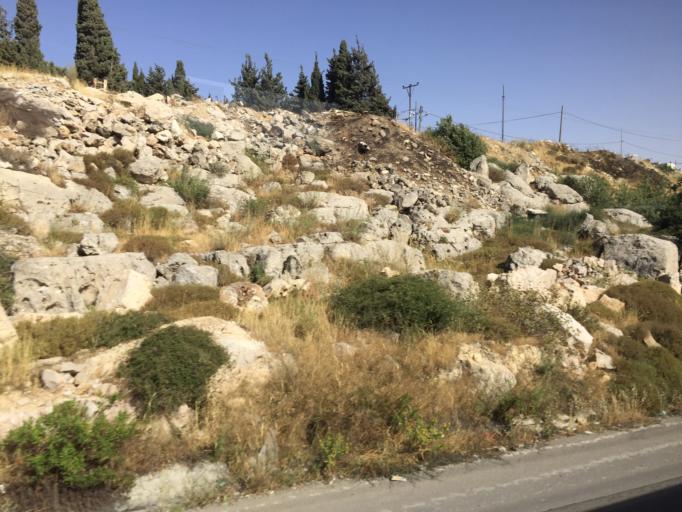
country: PS
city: Ad Dawhah
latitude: 31.7067
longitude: 35.1714
